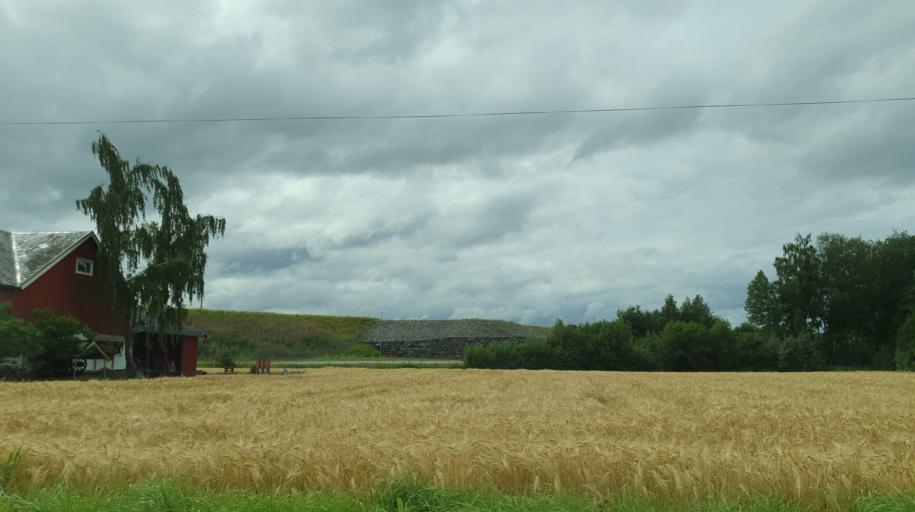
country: NO
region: Nord-Trondelag
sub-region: Stjordal
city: Stjordalshalsen
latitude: 63.4586
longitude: 10.9492
